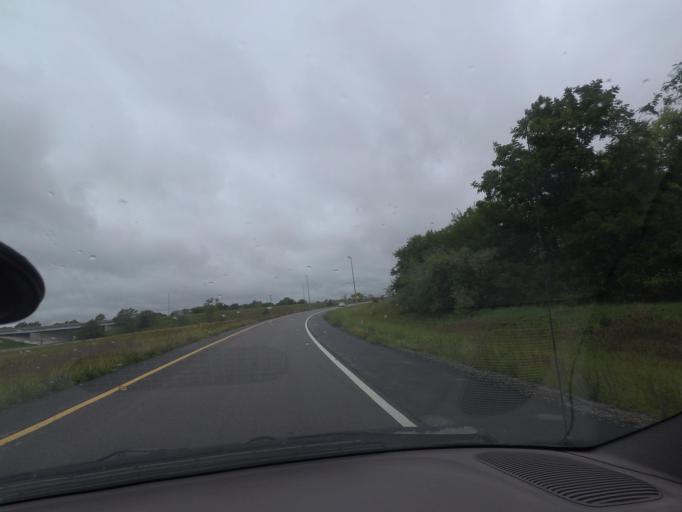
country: US
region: Illinois
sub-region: Macon County
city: Harristown
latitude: 39.8406
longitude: -89.0444
